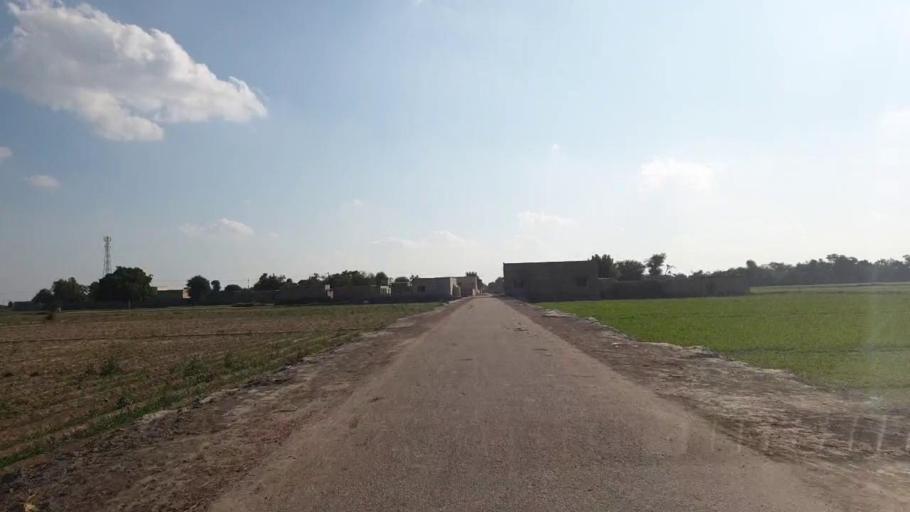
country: PK
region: Sindh
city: Shahpur Chakar
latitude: 26.1067
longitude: 68.5645
